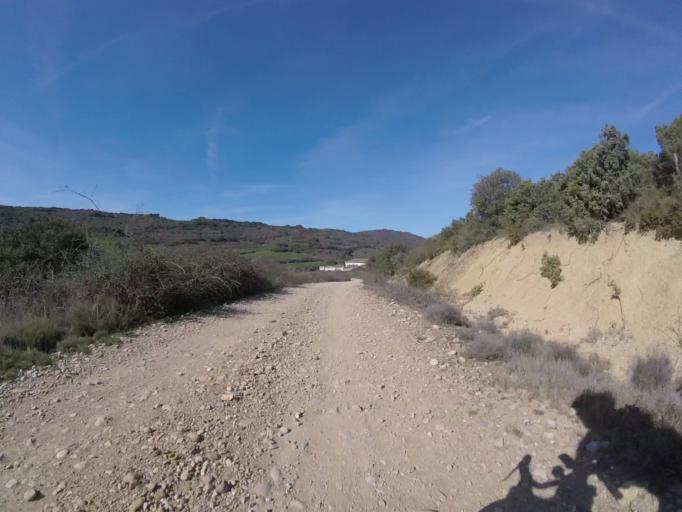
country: ES
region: Navarre
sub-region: Provincia de Navarra
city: Cirauqui
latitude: 42.6364
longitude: -1.8885
